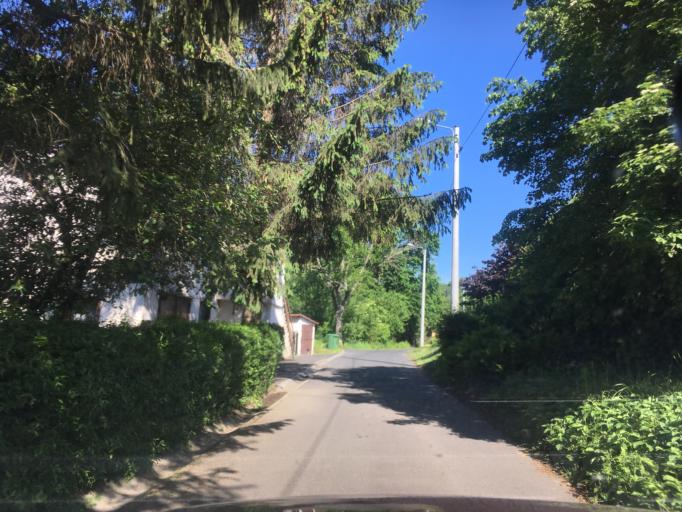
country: PL
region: Lower Silesian Voivodeship
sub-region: Powiat zgorzelecki
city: Sulikow
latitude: 51.0767
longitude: 15.0626
